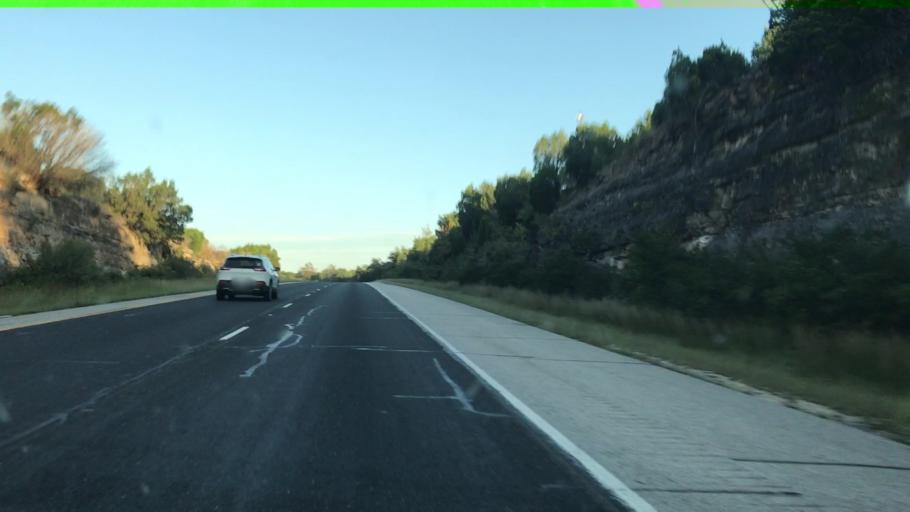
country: US
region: Texas
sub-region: Kerr County
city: Kerrville
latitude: 30.0682
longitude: -99.0769
